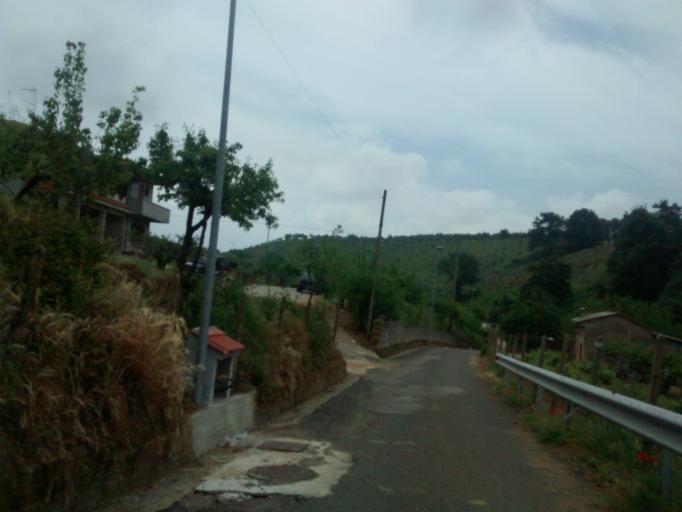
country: IT
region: Calabria
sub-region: Provincia di Catanzaro
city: Cortale
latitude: 38.8854
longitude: 16.4081
